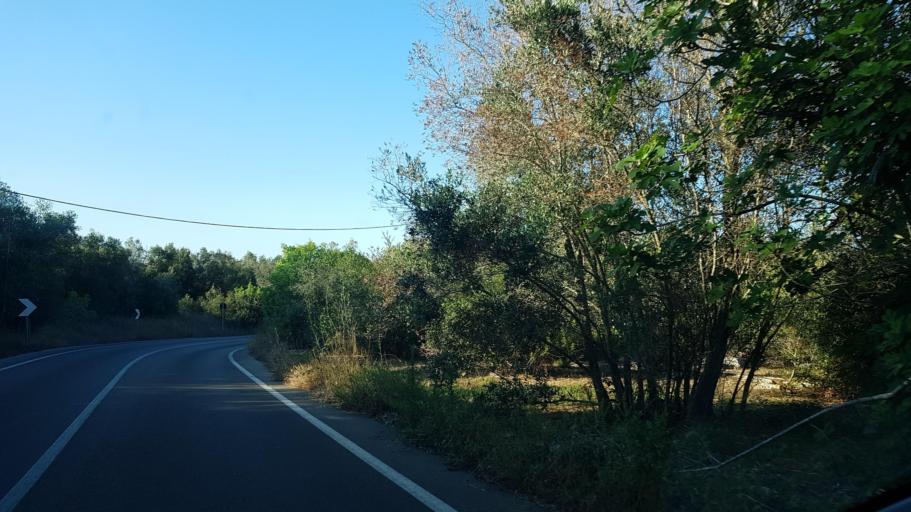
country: IT
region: Apulia
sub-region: Provincia di Lecce
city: Castro
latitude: 40.0055
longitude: 18.4153
